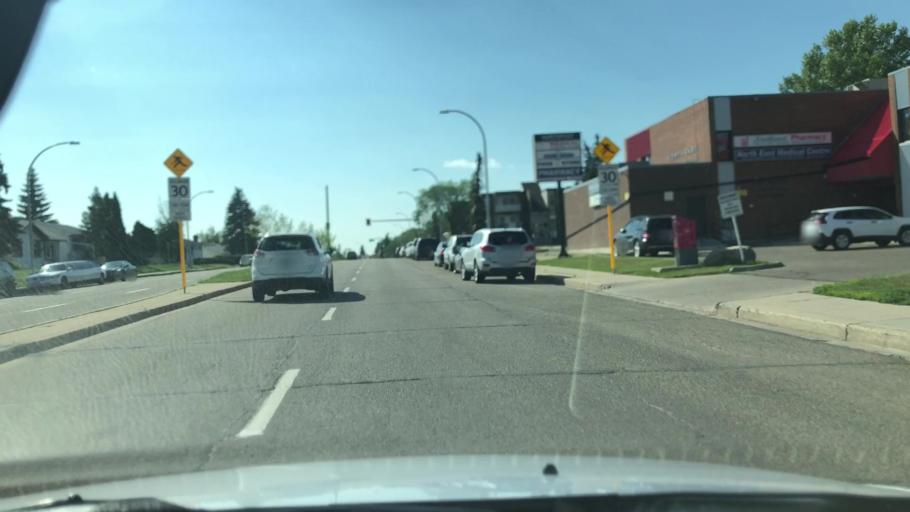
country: CA
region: Alberta
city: Edmonton
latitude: 53.6060
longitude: -113.4513
